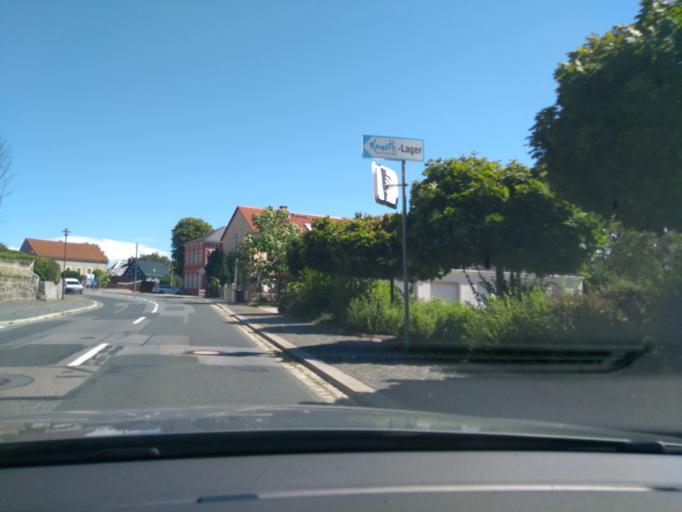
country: DE
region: Saxony
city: Hauswalde
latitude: 51.1484
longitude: 14.0641
